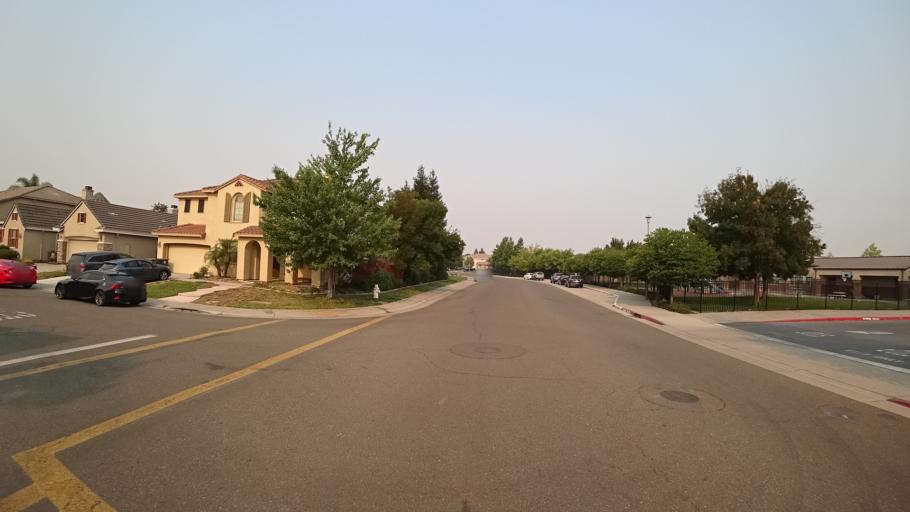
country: US
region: California
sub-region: Sacramento County
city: Laguna
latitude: 38.3993
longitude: -121.4416
